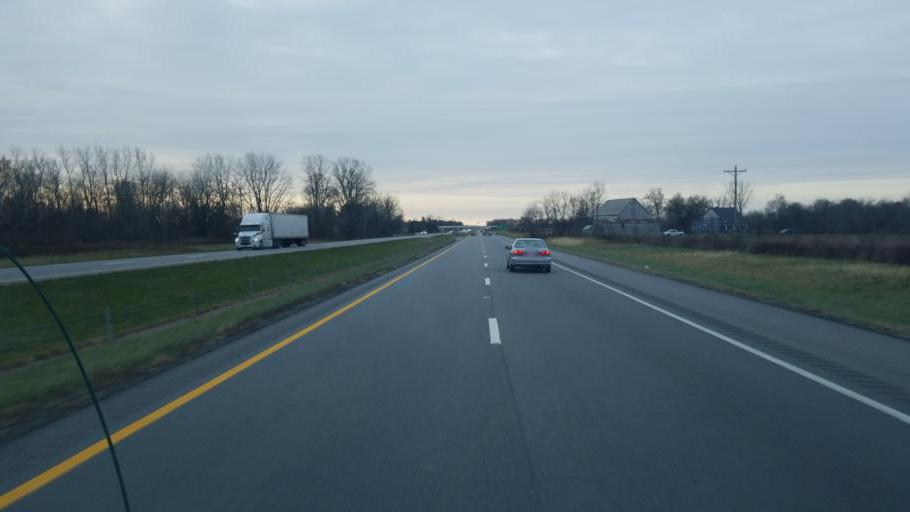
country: US
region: Ohio
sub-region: Auglaize County
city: Wapakoneta
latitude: 40.5934
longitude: -84.1612
